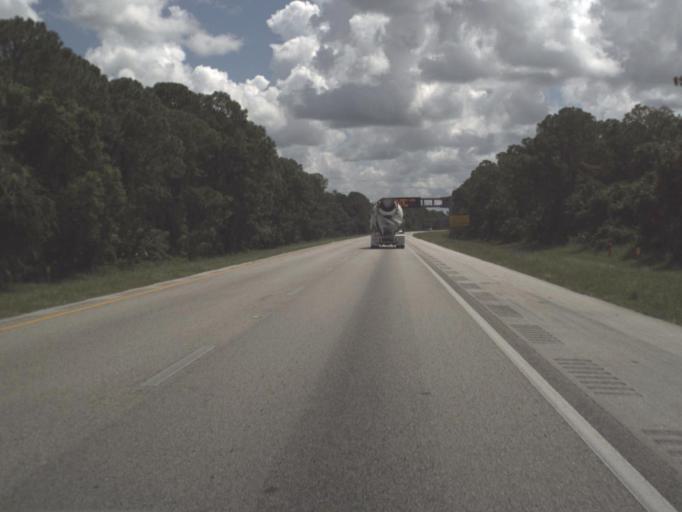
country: US
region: Florida
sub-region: Collier County
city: Golden Gate
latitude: 26.1636
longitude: -81.7080
